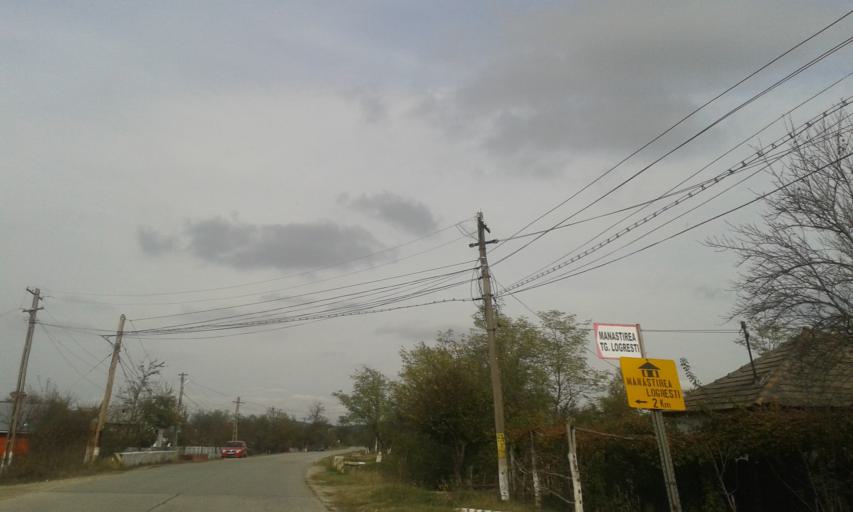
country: RO
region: Gorj
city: Logresti
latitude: 44.8656
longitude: 23.7020
